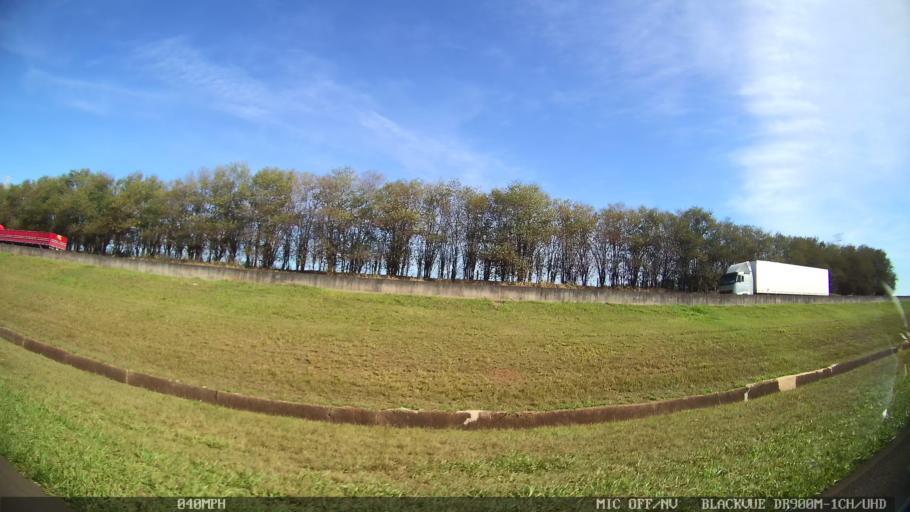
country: BR
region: Sao Paulo
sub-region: Leme
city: Leme
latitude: -22.2641
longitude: -47.3908
